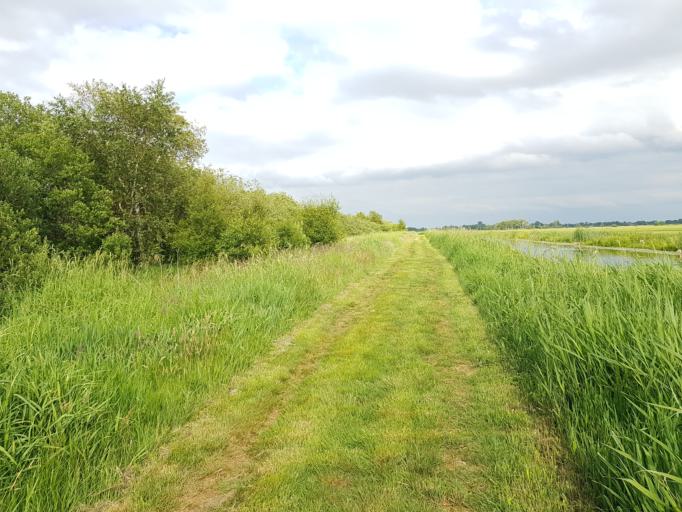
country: NL
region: Friesland
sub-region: Gemeente Smallingerland
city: Oudega
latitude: 53.0857
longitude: 5.9576
